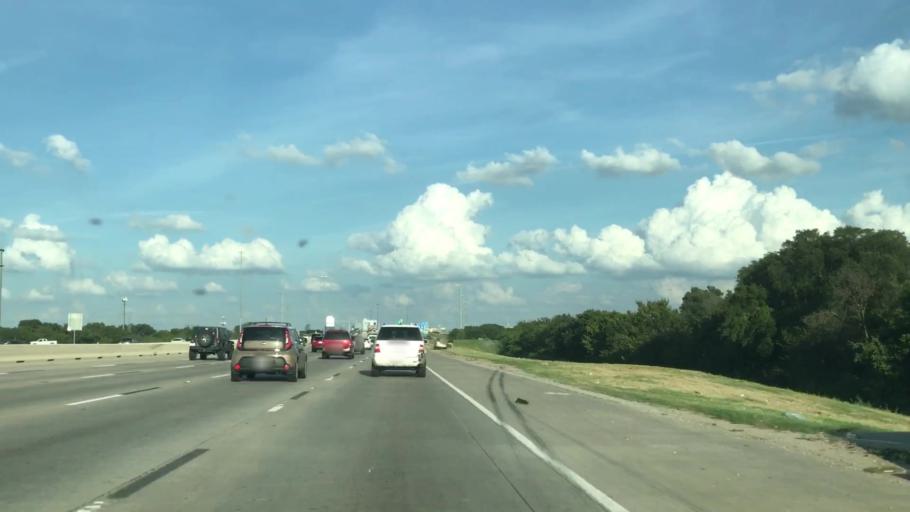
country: US
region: Texas
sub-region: Dallas County
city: Cockrell Hill
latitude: 32.7654
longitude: -96.9260
